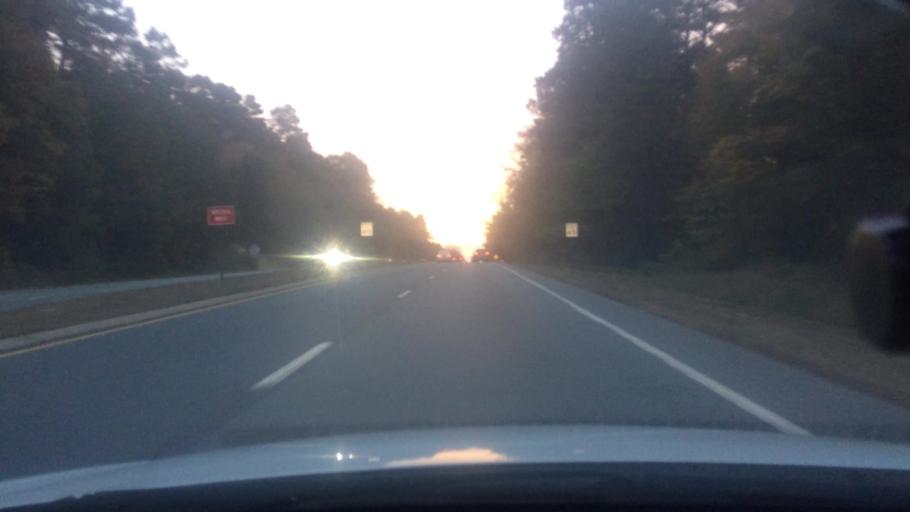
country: US
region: North Carolina
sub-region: Orange County
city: Chapel Hill
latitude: 35.8950
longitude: -79.0496
